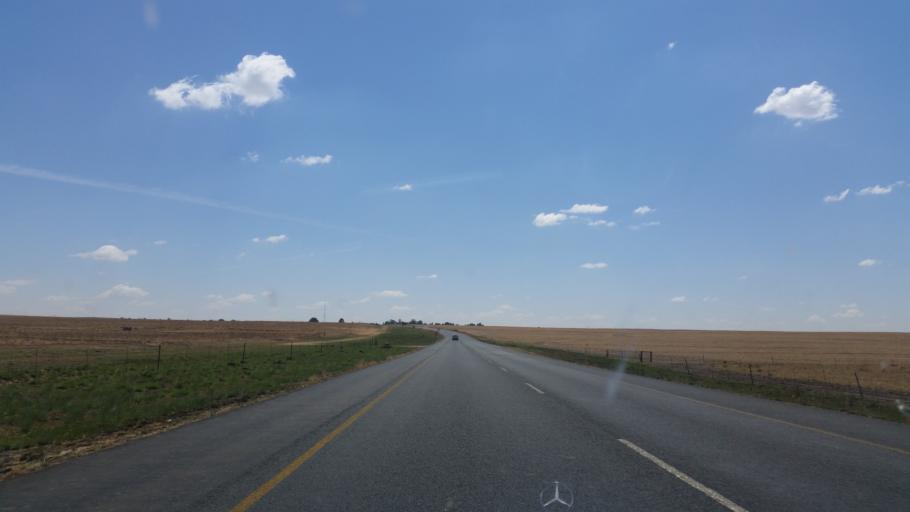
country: ZA
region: Orange Free State
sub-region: Thabo Mofutsanyana District Municipality
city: Reitz
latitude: -28.0909
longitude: 28.6540
